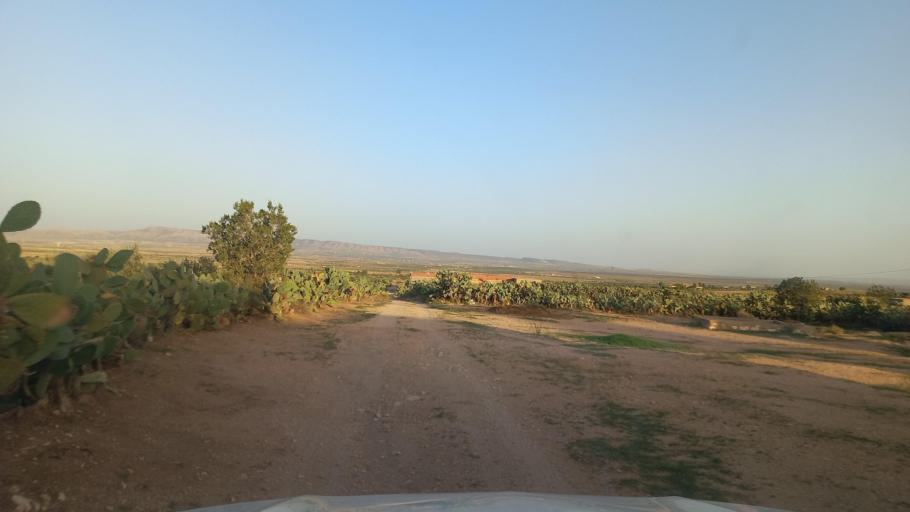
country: TN
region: Al Qasrayn
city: Sbiba
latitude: 35.3732
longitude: 9.0095
